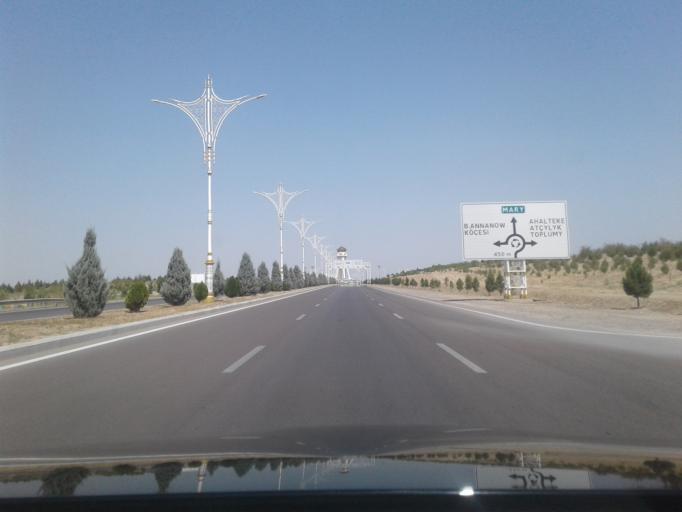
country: TM
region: Ahal
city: Ashgabat
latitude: 37.8781
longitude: 58.4155
